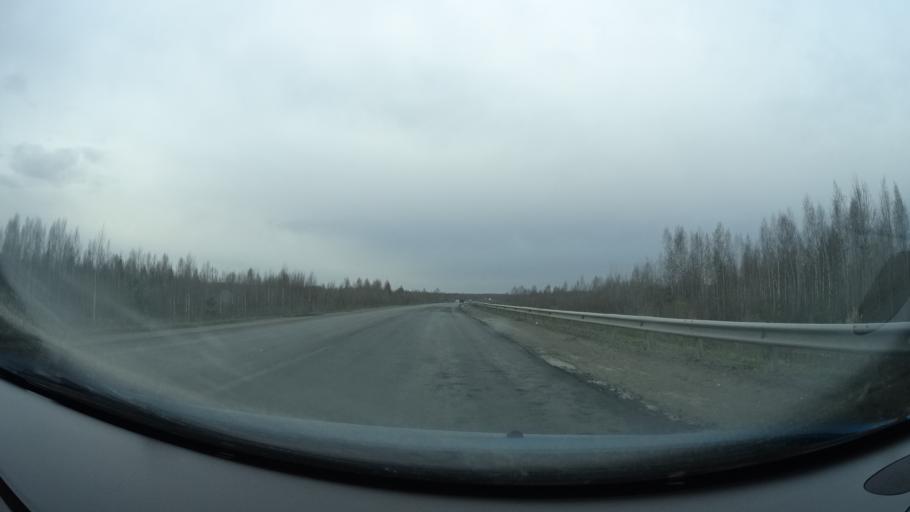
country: RU
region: Perm
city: Krasnokamsk
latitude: 58.0920
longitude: 55.7289
